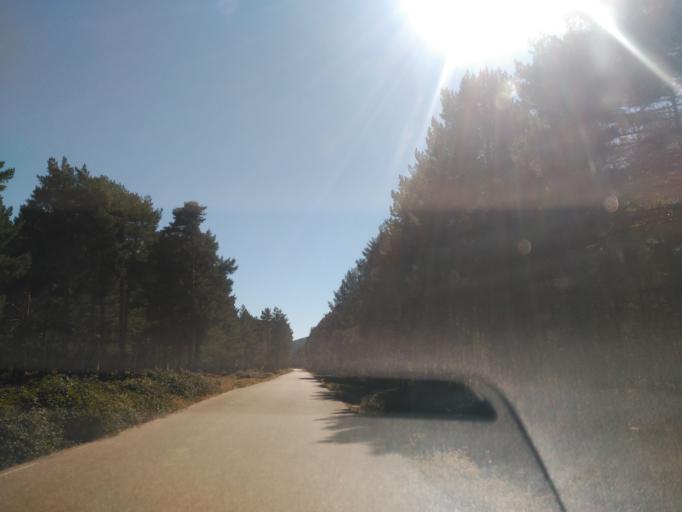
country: ES
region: Castille and Leon
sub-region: Provincia de Soria
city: Vinuesa
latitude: 41.9470
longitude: -2.7807
